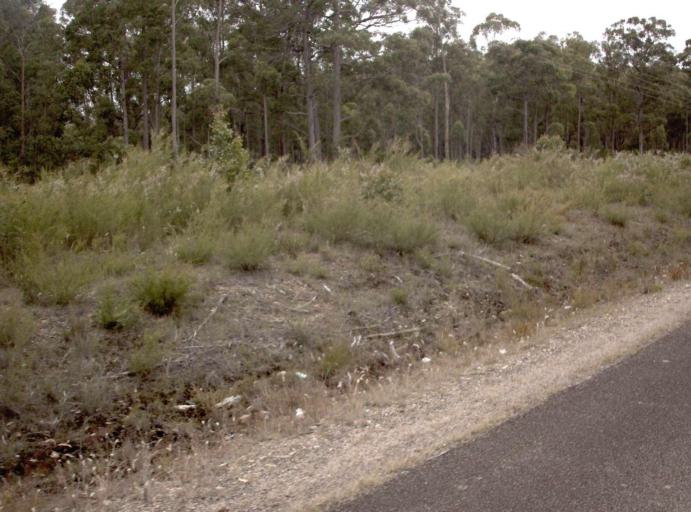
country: AU
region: Victoria
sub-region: East Gippsland
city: Lakes Entrance
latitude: -37.7158
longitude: 147.9719
